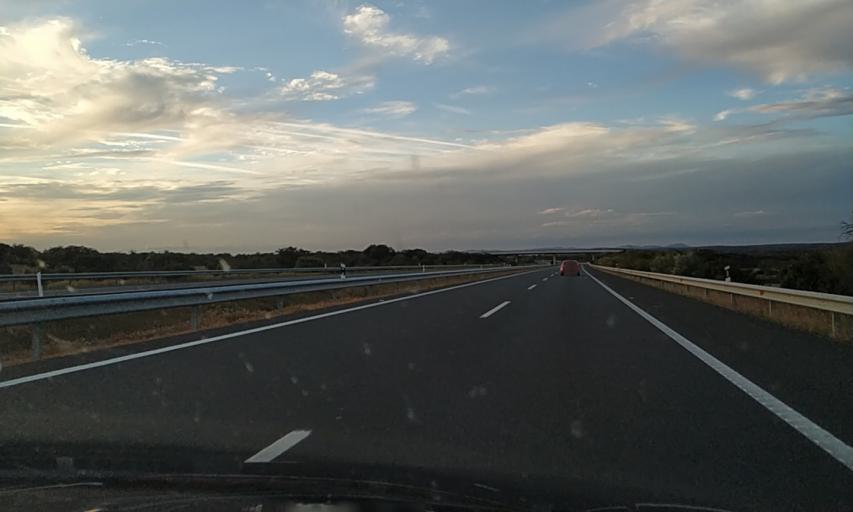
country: ES
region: Extremadura
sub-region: Provincia de Caceres
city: Alcuescar
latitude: 39.1871
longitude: -6.2763
